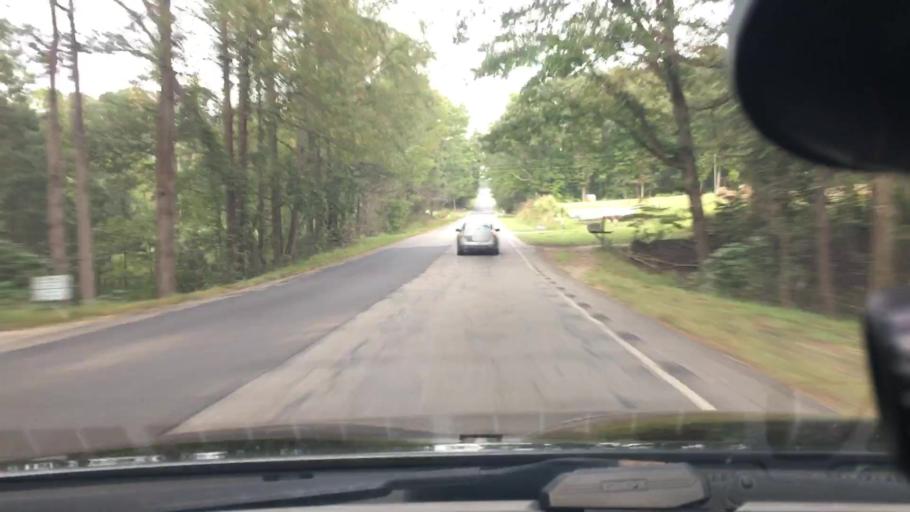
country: US
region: North Carolina
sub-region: Moore County
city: Carthage
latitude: 35.3737
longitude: -79.2984
